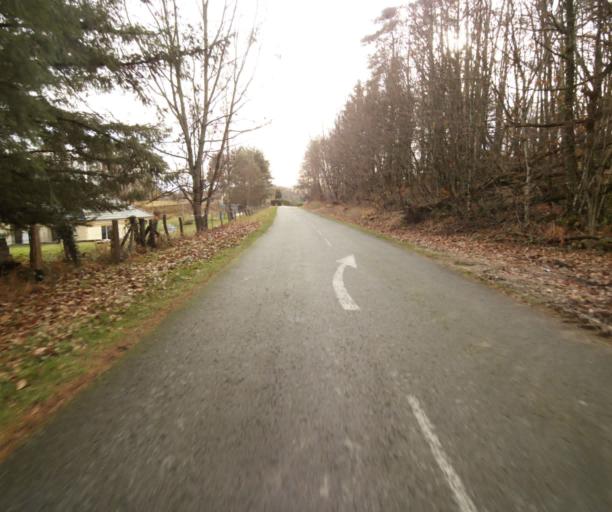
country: FR
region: Limousin
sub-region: Departement de la Correze
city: Chameyrat
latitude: 45.2437
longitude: 1.6989
